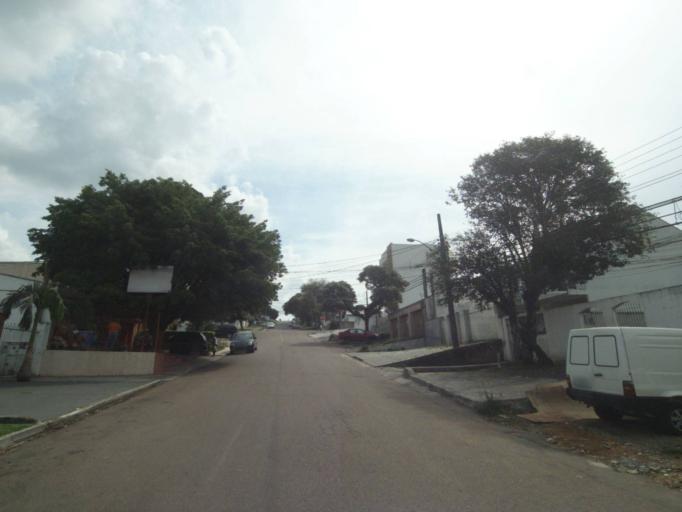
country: BR
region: Parana
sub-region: Pinhais
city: Pinhais
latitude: -25.4044
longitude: -49.2094
